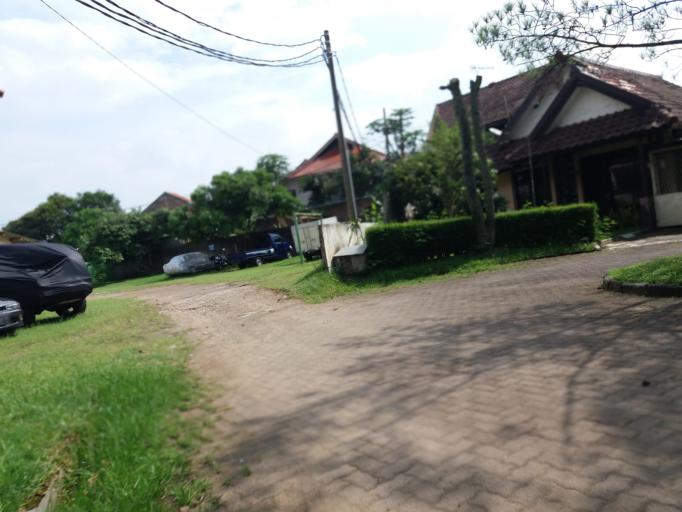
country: ID
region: West Java
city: Bandung
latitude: -6.9175
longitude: 107.6528
